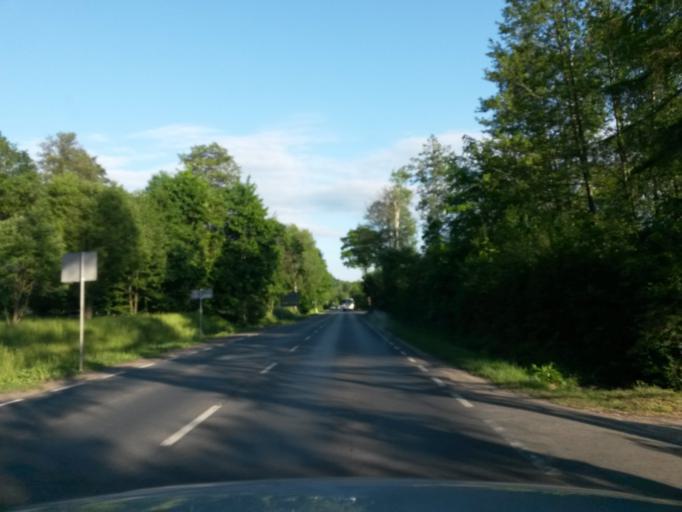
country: PL
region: Lower Silesian Voivodeship
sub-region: Jelenia Gora
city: Jelenia Gora
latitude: 50.8869
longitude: 15.7556
